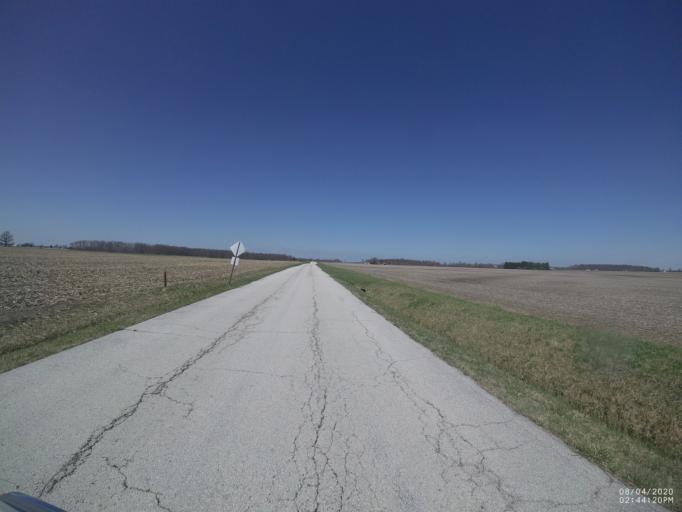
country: US
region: Ohio
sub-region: Sandusky County
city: Gibsonburg
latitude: 41.2915
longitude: -83.2958
